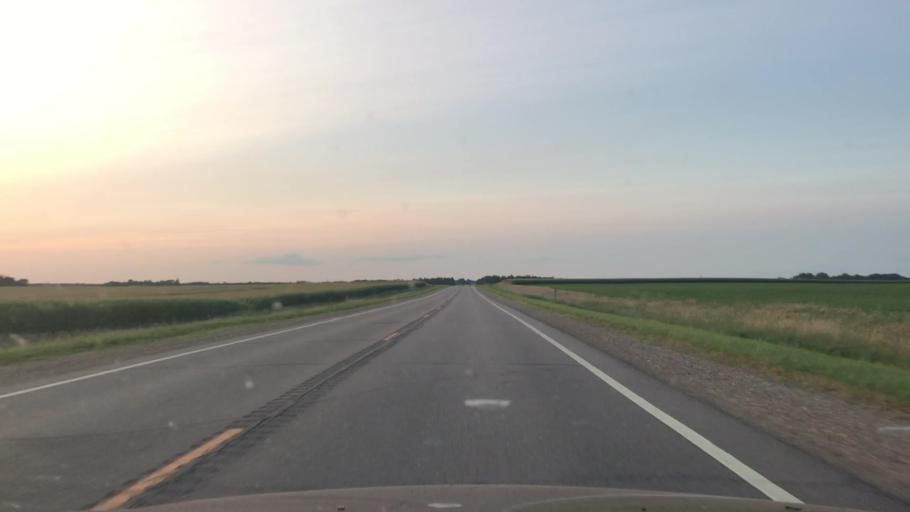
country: US
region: Minnesota
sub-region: Redwood County
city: Redwood Falls
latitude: 44.5033
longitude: -95.1178
